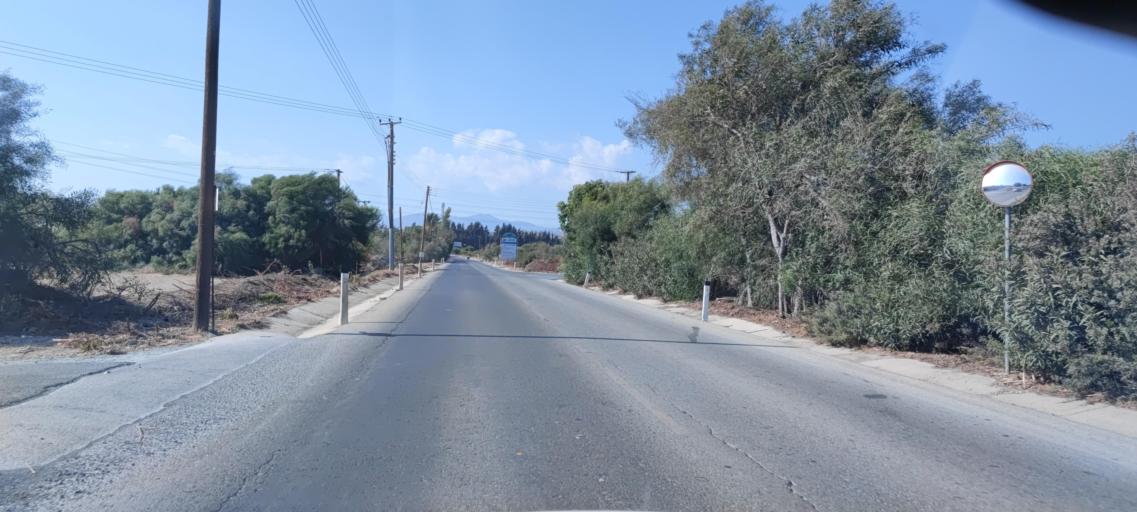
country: CY
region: Larnaka
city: Kofinou
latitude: 34.7371
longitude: 33.3322
